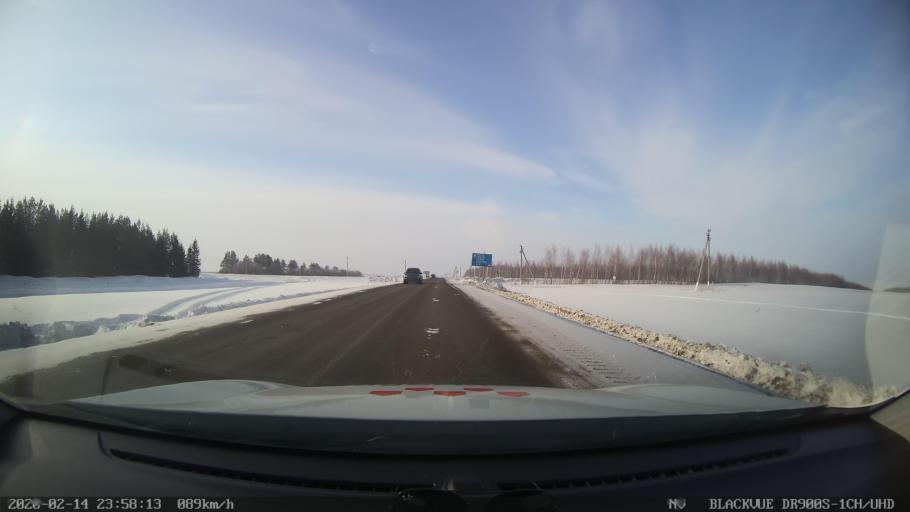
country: RU
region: Tatarstan
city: Kuybyshevskiy Zaton
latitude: 55.3394
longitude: 49.0923
